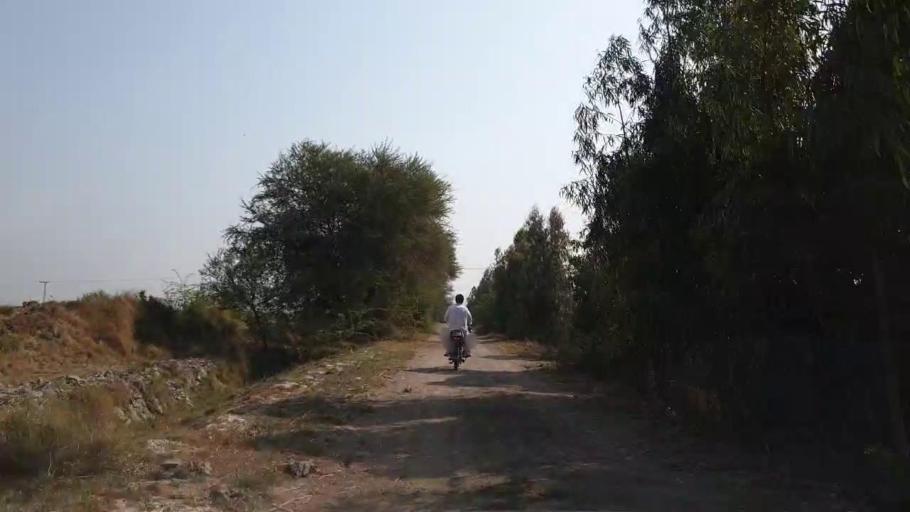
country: PK
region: Sindh
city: Mirpur Khas
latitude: 25.6051
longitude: 69.0200
